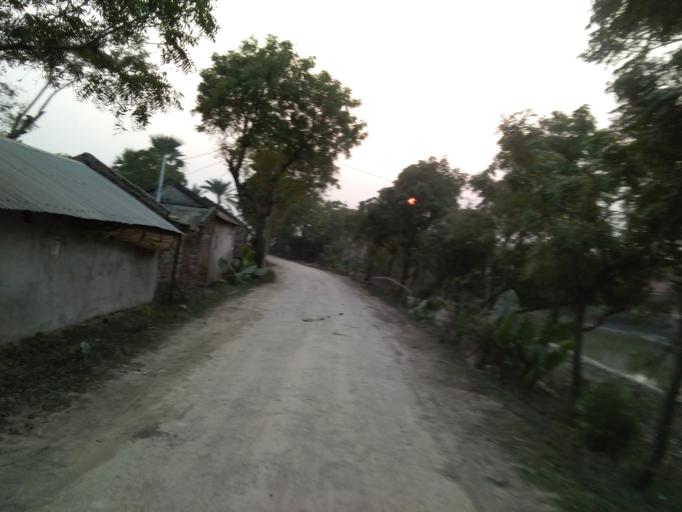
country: BD
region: Khulna
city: Satkhira
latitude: 22.6513
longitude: 89.0153
